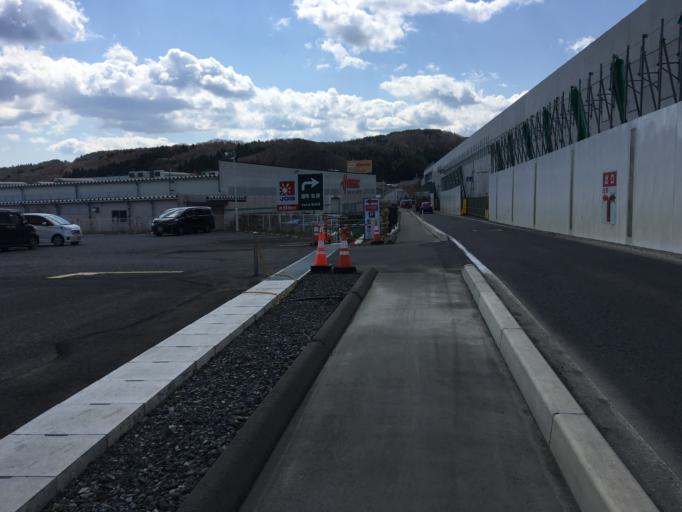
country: JP
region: Aomori
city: Hachinohe
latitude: 40.1906
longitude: 141.7871
